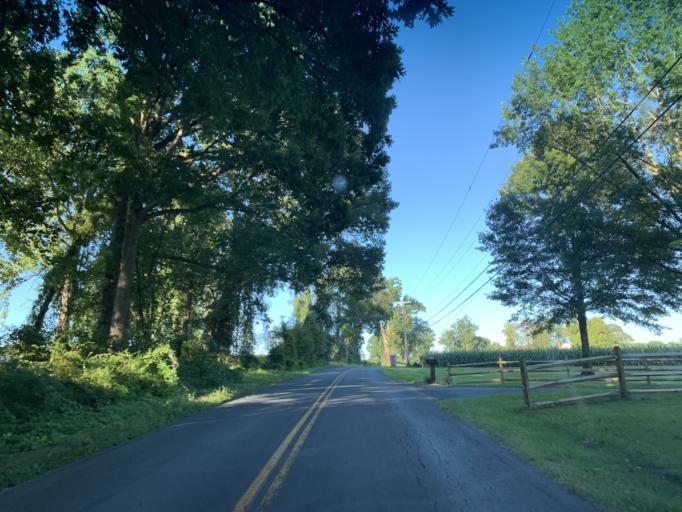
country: US
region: Maryland
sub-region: Harford County
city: Jarrettsville
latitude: 39.5916
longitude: -76.4450
